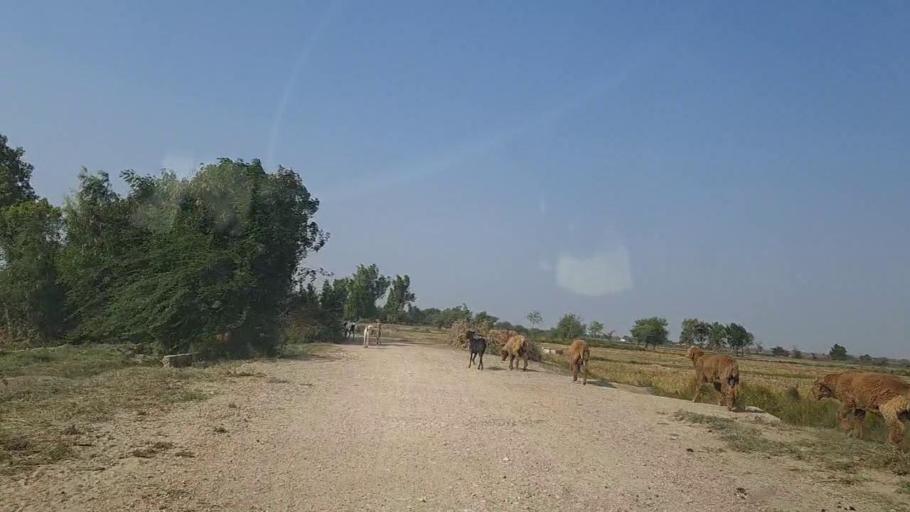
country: PK
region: Sindh
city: Mirpur Sakro
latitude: 24.5657
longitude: 67.8272
